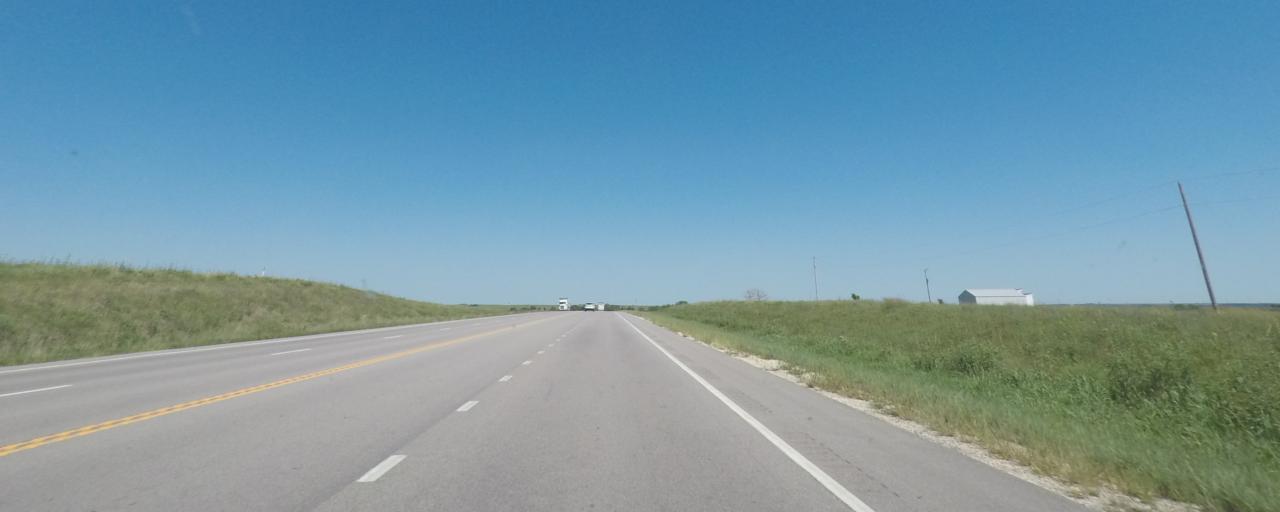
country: US
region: Kansas
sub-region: Chase County
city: Cottonwood Falls
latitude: 38.4023
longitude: -96.4999
